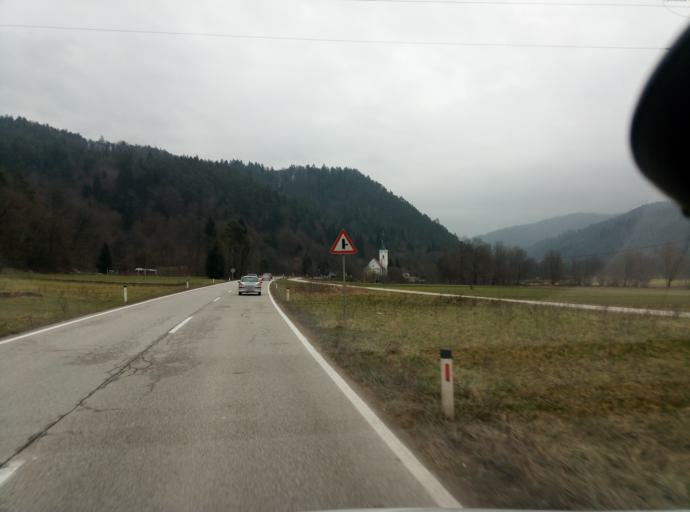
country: SI
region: Moravce
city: Moravce
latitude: 46.0962
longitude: 14.6874
